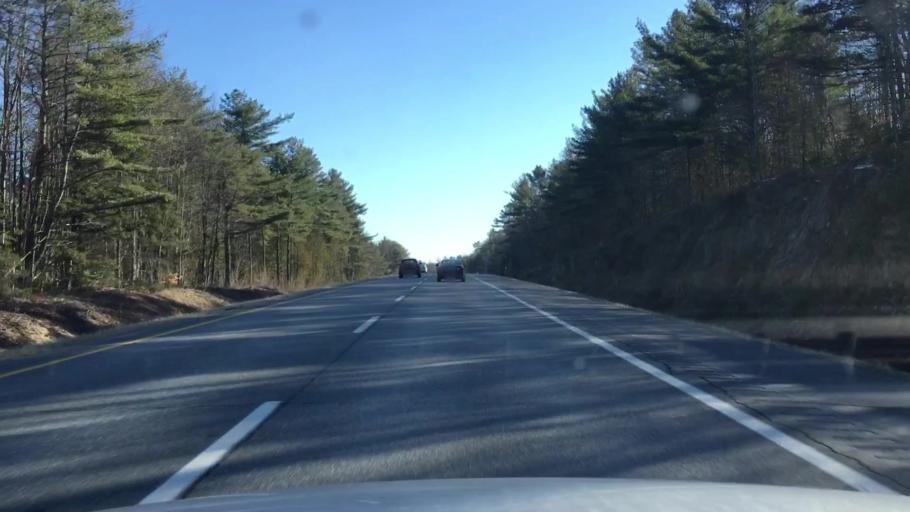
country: US
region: Maine
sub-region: Penobscot County
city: Plymouth
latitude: 44.7975
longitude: -69.2137
